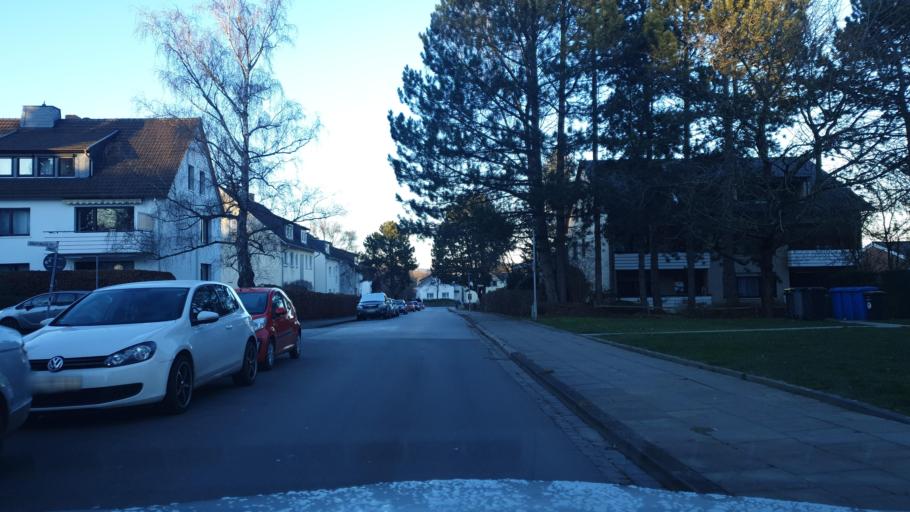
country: DE
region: North Rhine-Westphalia
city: Bad Oeynhausen
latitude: 52.1935
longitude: 8.8072
